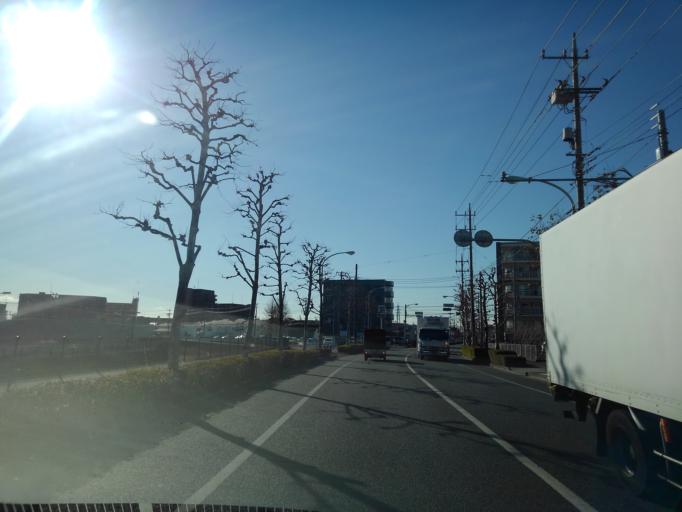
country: JP
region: Tokyo
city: Fussa
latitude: 35.7322
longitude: 139.3830
